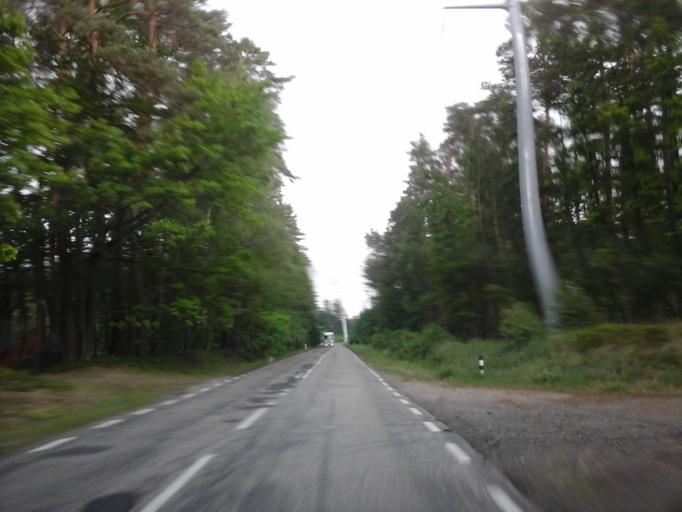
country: PL
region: West Pomeranian Voivodeship
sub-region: Powiat drawski
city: Czaplinek
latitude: 53.4821
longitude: 16.2280
